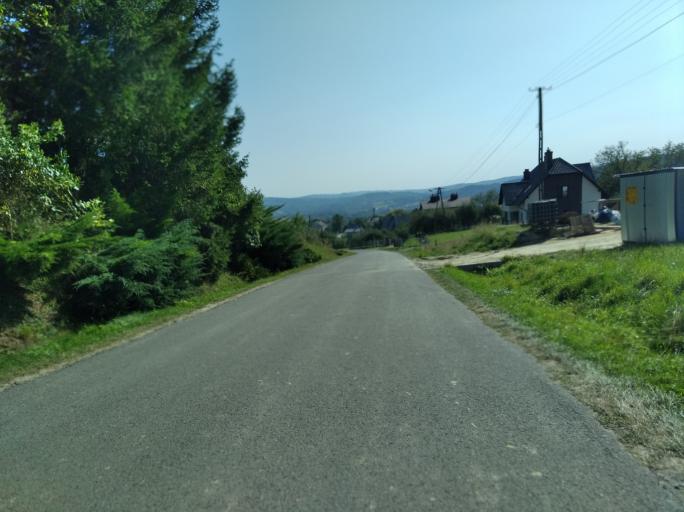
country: PL
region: Subcarpathian Voivodeship
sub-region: Powiat strzyzowski
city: Czudec
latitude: 49.9536
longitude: 21.8303
